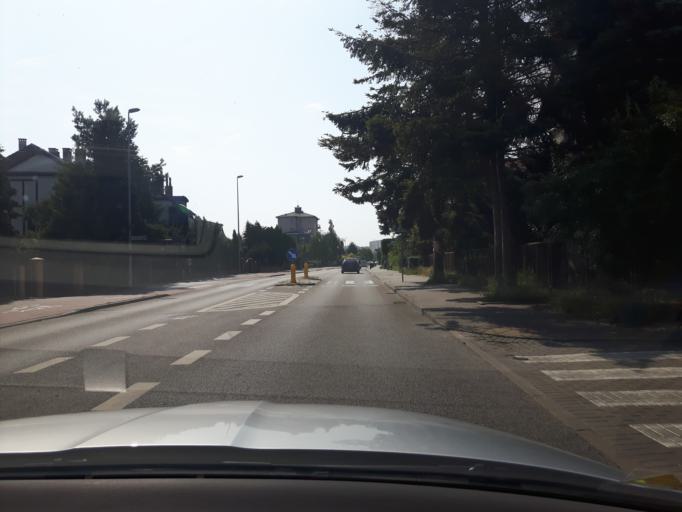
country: PL
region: Pomeranian Voivodeship
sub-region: Sopot
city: Sopot
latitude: 54.4310
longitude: 18.5731
